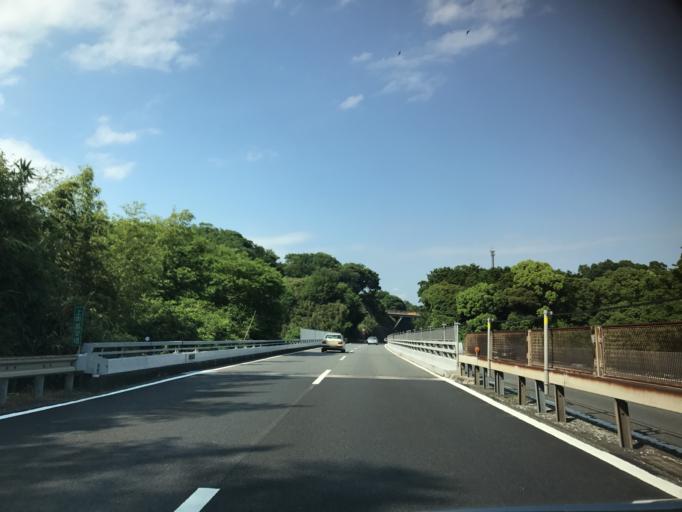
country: JP
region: Kanagawa
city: Ninomiya
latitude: 35.2998
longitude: 139.2175
